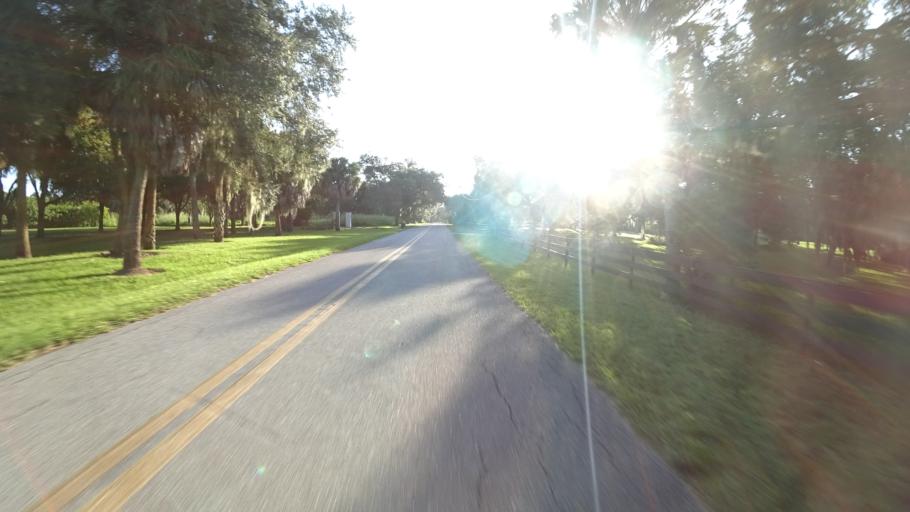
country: US
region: Florida
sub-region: Manatee County
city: Memphis
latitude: 27.5722
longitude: -82.5836
